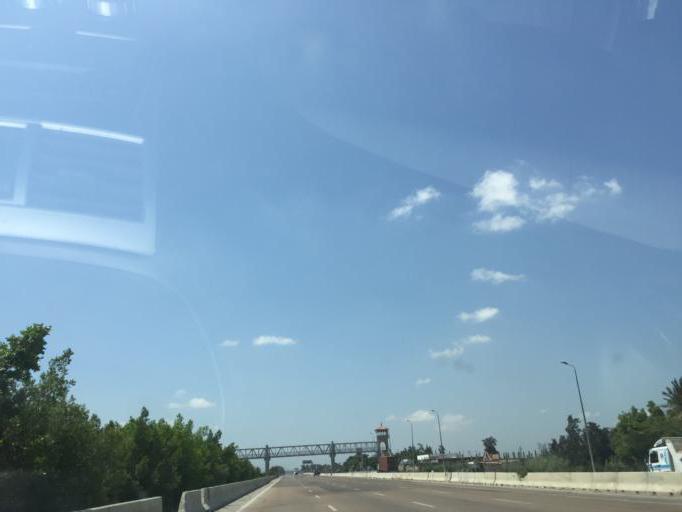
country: EG
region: Alexandria
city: Alexandria
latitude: 30.9445
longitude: 29.8445
